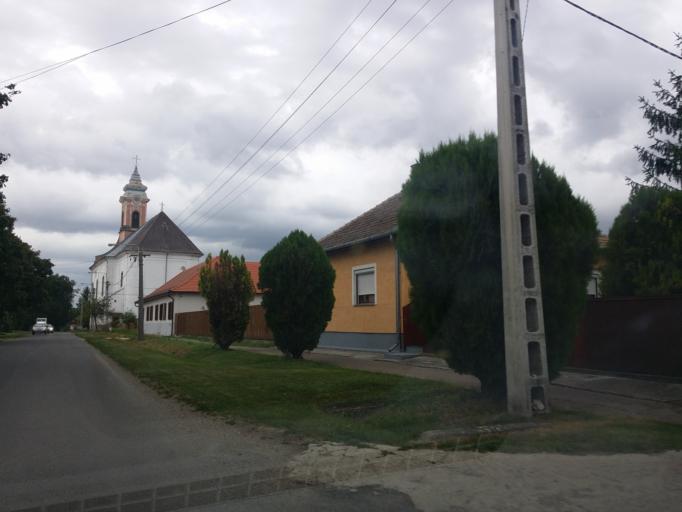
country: HU
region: Heves
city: Tiszanana
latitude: 47.5870
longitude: 20.5977
